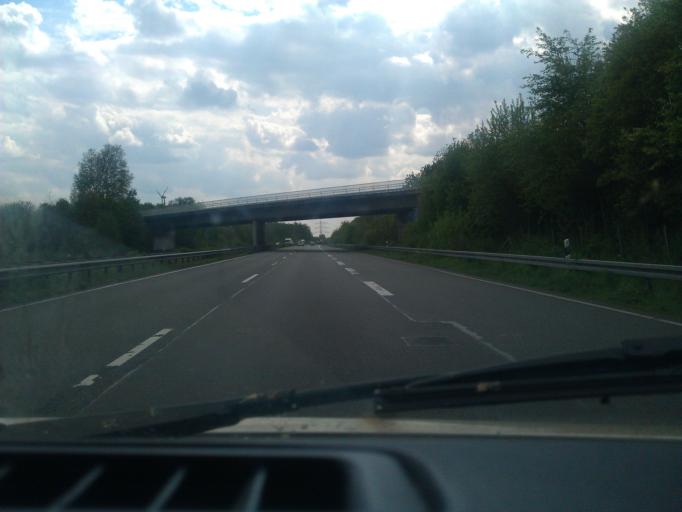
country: DE
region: North Rhine-Westphalia
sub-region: Regierungsbezirk Munster
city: Ochtrup
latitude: 52.2506
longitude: 7.1665
